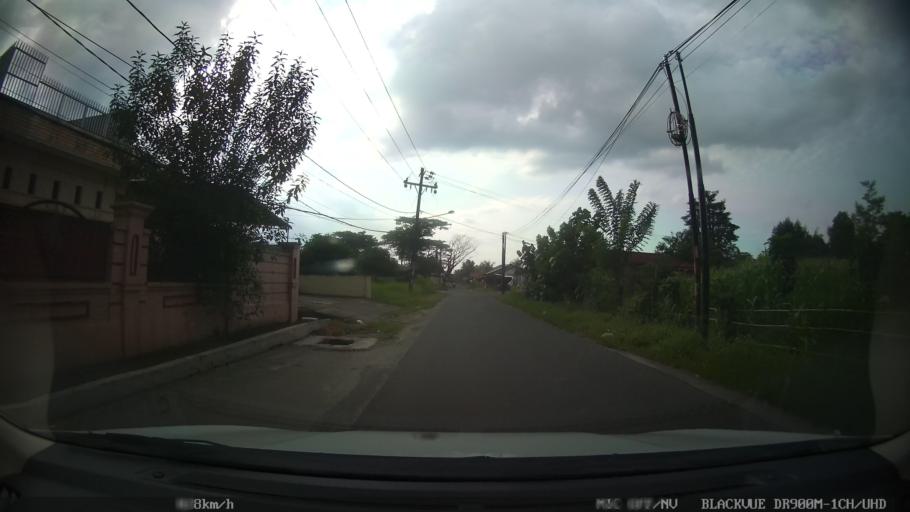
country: ID
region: North Sumatra
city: Sunggal
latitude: 3.5314
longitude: 98.6059
